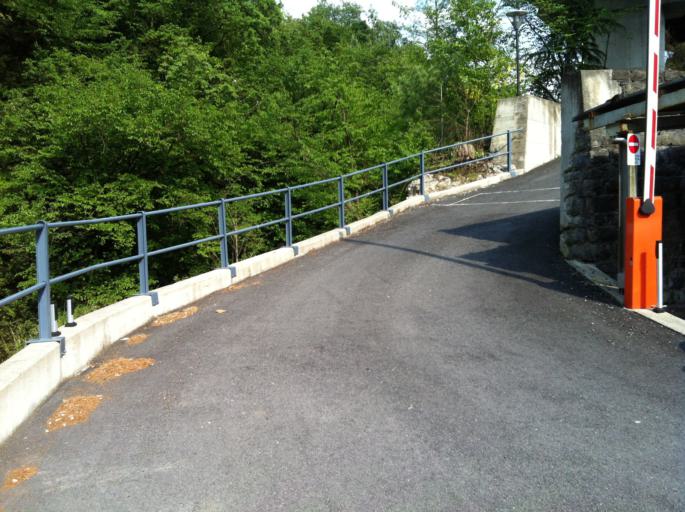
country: IT
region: Lombardy
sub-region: Provincia di Como
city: Menaggio
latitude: 46.0235
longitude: 9.2324
